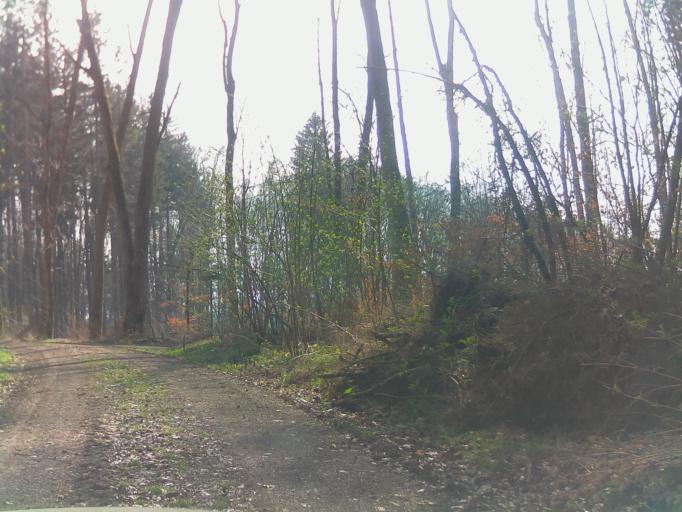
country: DE
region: Bavaria
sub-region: Swabia
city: Altenstadt
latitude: 48.1734
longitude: 10.1345
